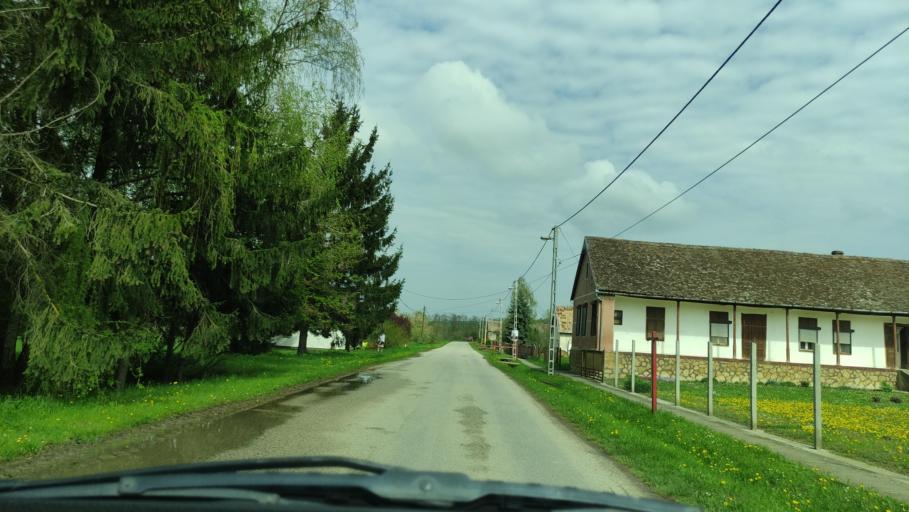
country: HU
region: Baranya
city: Magocs
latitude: 46.2780
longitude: 18.2079
